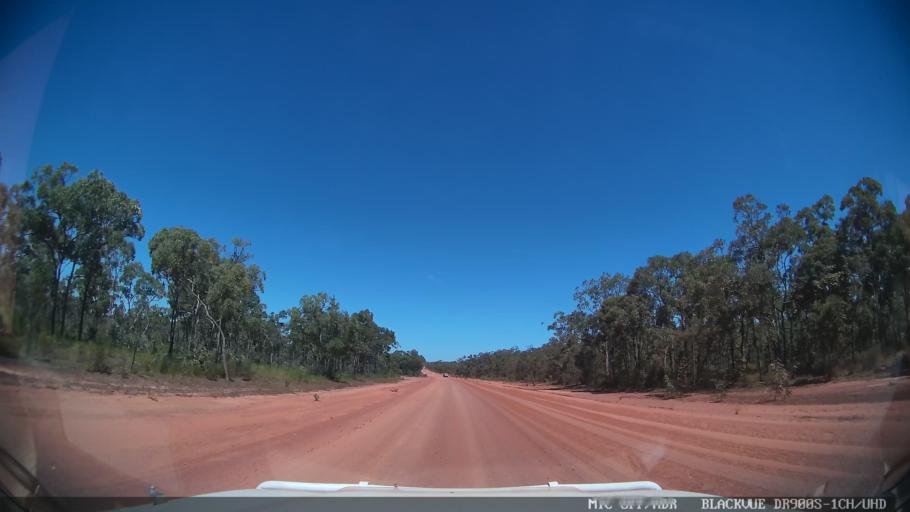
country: AU
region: Queensland
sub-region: Torres
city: Thursday Island
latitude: -11.3644
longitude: 142.3460
